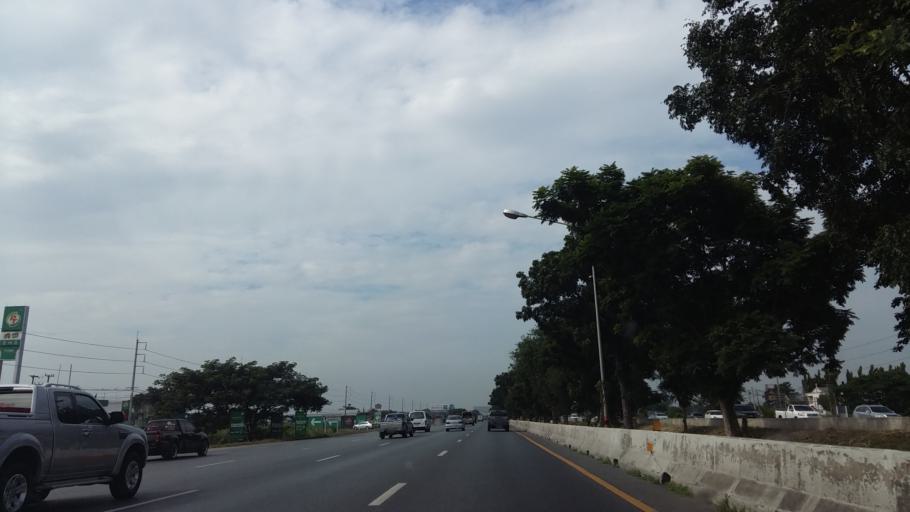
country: TH
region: Phra Nakhon Si Ayutthaya
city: Bang Pahan
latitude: 14.4838
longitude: 100.5288
